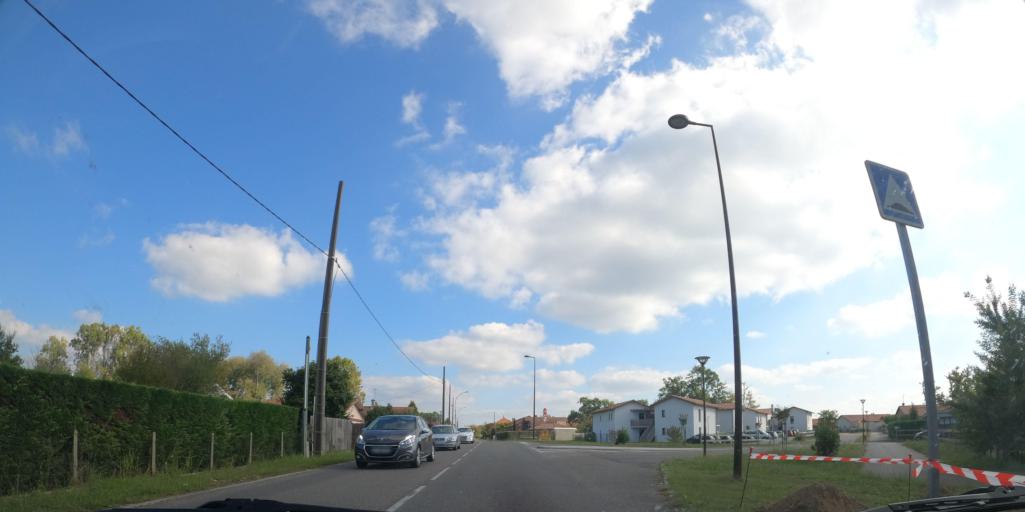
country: FR
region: Aquitaine
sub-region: Departement des Landes
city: Soustons
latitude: 43.7466
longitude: -1.3149
